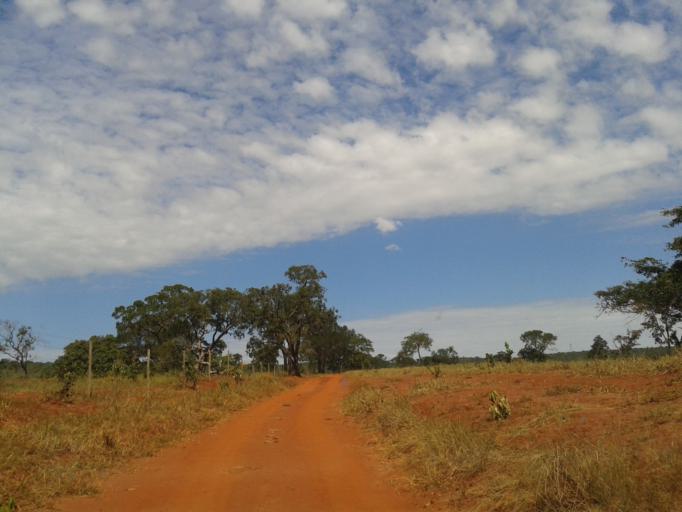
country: BR
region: Minas Gerais
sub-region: Campina Verde
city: Campina Verde
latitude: -19.3965
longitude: -49.7660
